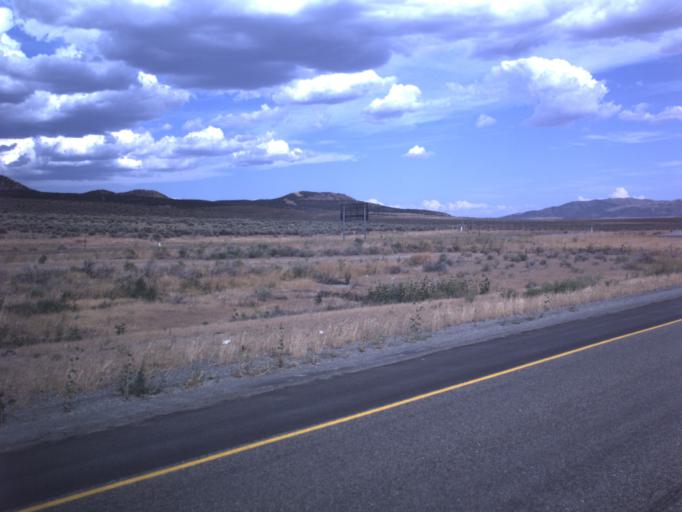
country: US
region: Idaho
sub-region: Oneida County
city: Malad City
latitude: 42.0000
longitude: -112.8342
